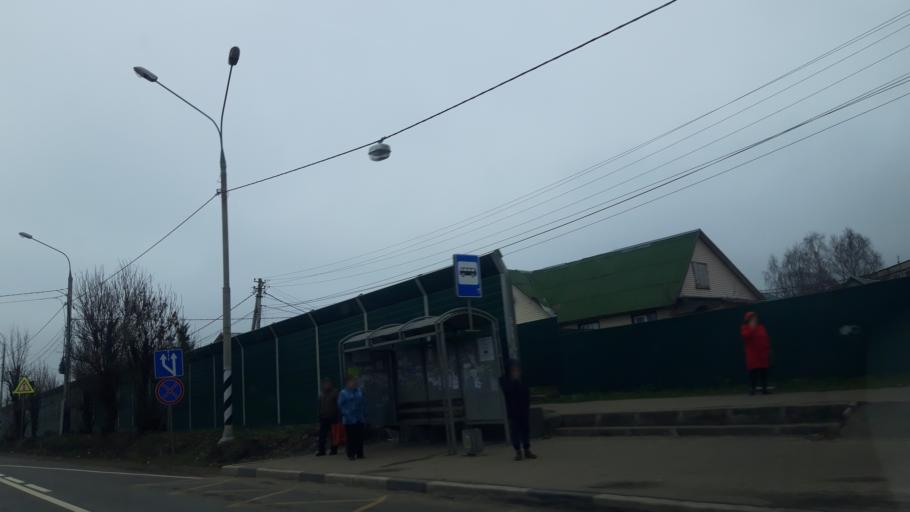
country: RU
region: Moskovskaya
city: Lozhki
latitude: 56.0925
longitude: 37.1099
